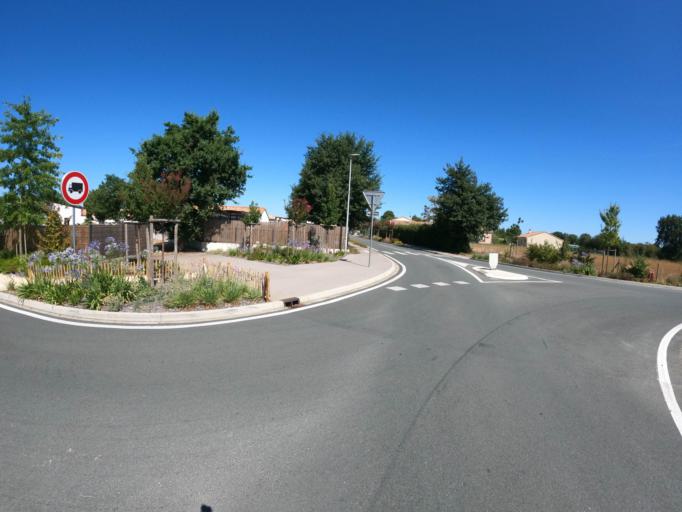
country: FR
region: Pays de la Loire
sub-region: Departement de la Vendee
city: Les Landes-Genusson
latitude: 46.9614
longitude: -1.1271
